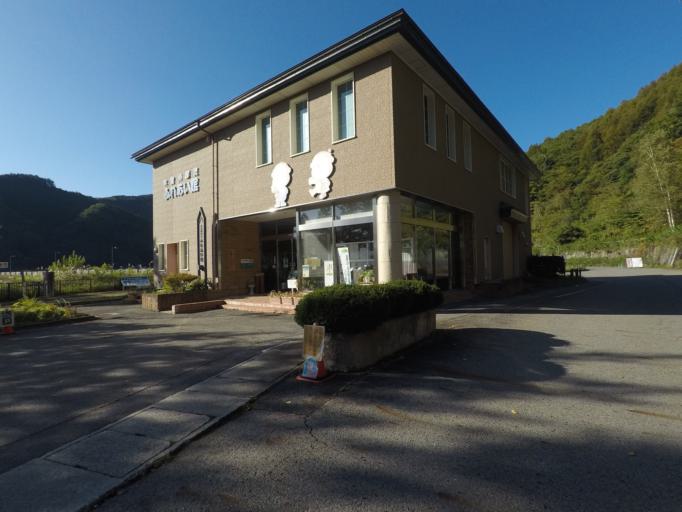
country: JP
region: Nagano
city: Tatsuno
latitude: 35.9764
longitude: 137.7730
